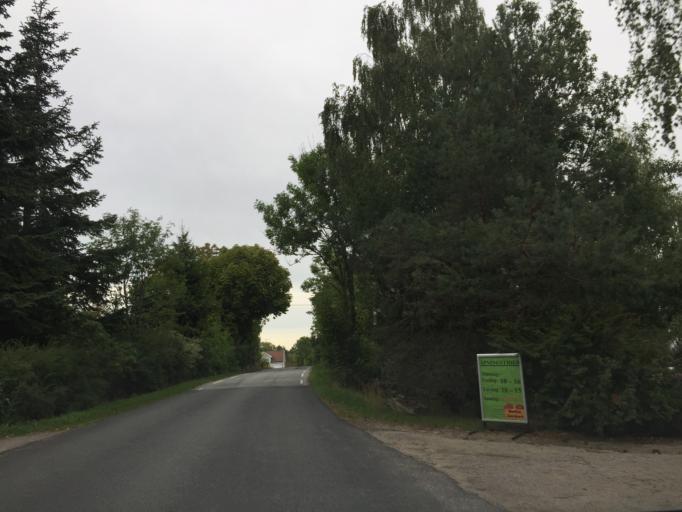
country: NO
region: Ostfold
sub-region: Hvaler
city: Skjaerhalden
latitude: 59.0617
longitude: 11.0335
